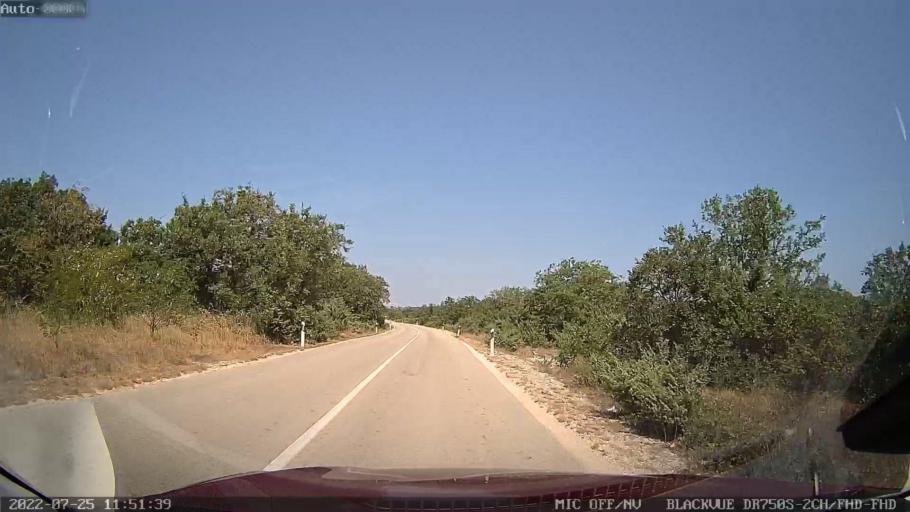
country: HR
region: Zadarska
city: Vrsi
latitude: 44.2409
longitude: 15.2505
